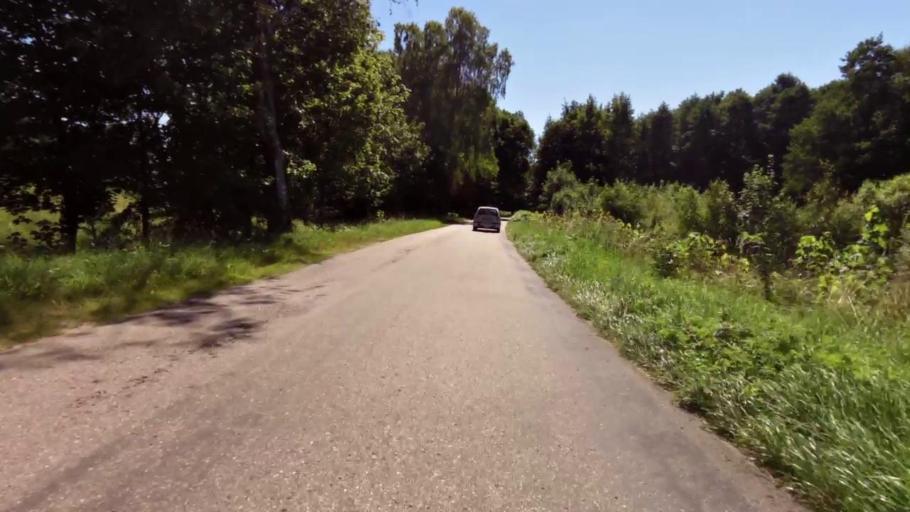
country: PL
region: West Pomeranian Voivodeship
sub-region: Powiat szczecinecki
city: Bialy Bor
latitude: 53.9656
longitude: 16.8657
